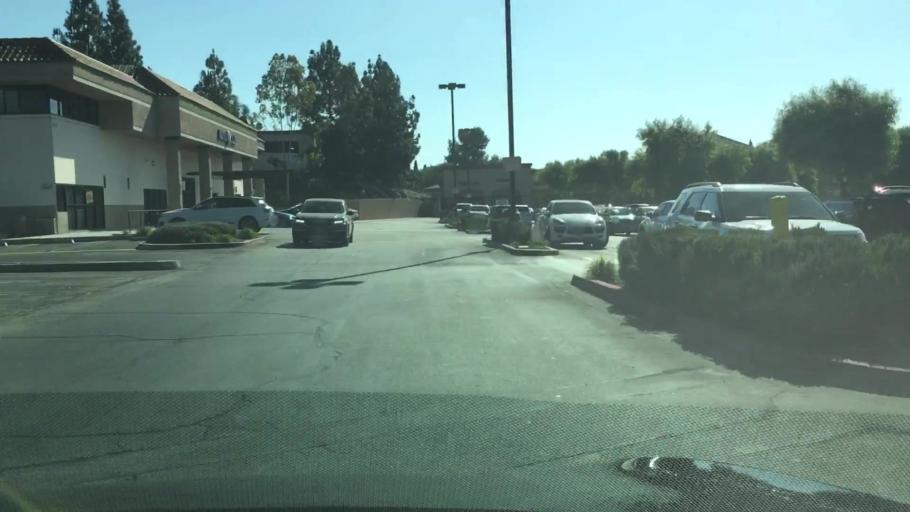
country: US
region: California
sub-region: Los Angeles County
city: Walnut
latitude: 33.9744
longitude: -117.8383
